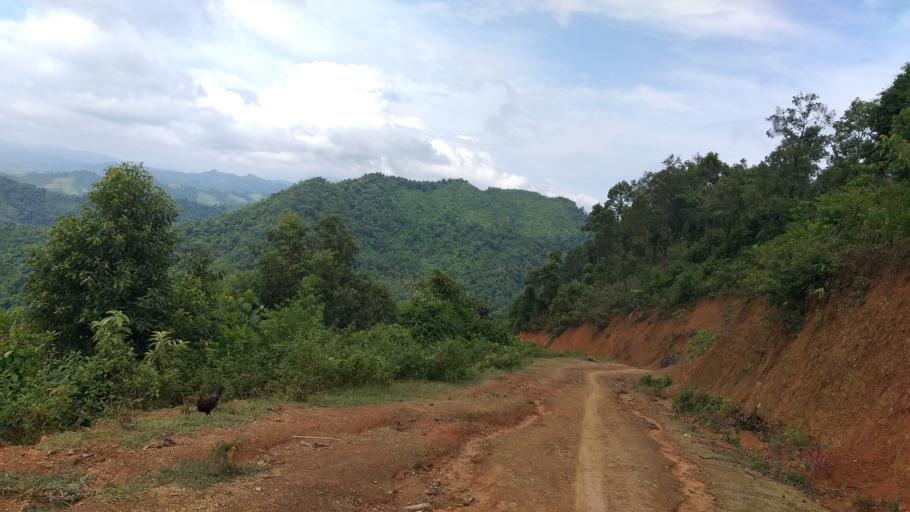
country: VN
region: Huyen Dien Bien
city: Dien Bien Phu
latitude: 21.4269
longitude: 102.6791
